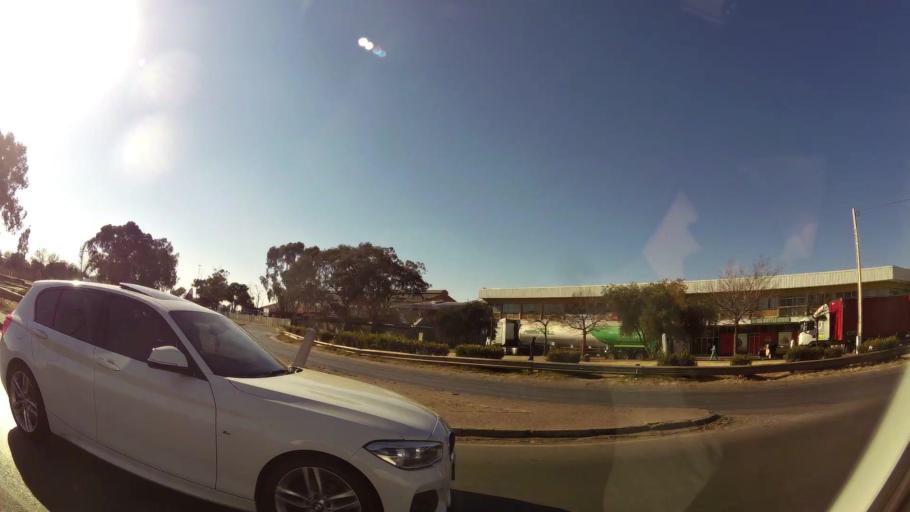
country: ZA
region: Gauteng
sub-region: Ekurhuleni Metropolitan Municipality
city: Germiston
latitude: -26.3002
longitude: 28.1173
